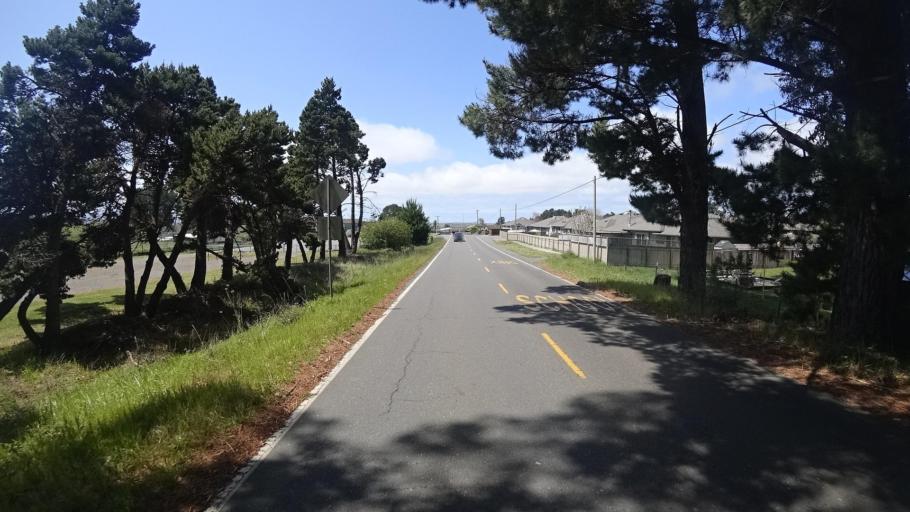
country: US
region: California
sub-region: Humboldt County
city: Fortuna
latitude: 40.6442
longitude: -124.2166
